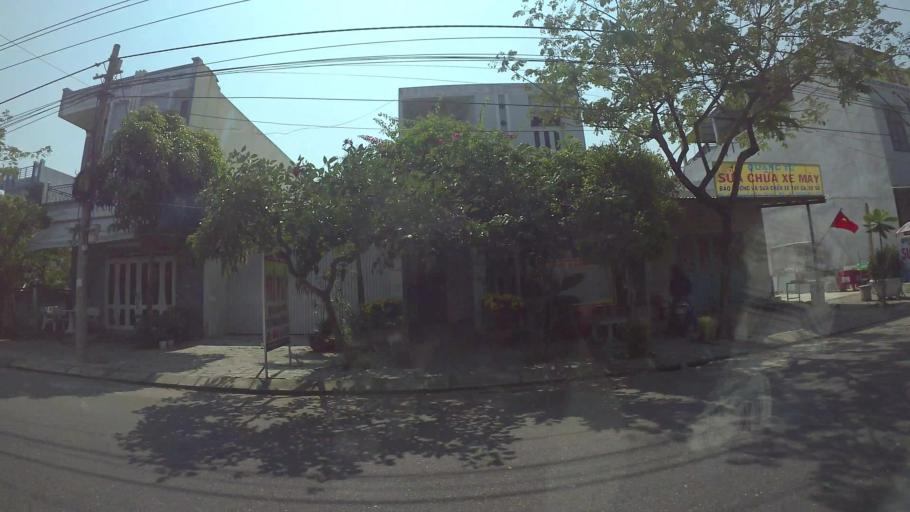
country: VN
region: Da Nang
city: Ngu Hanh Son
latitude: 15.9813
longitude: 108.2736
